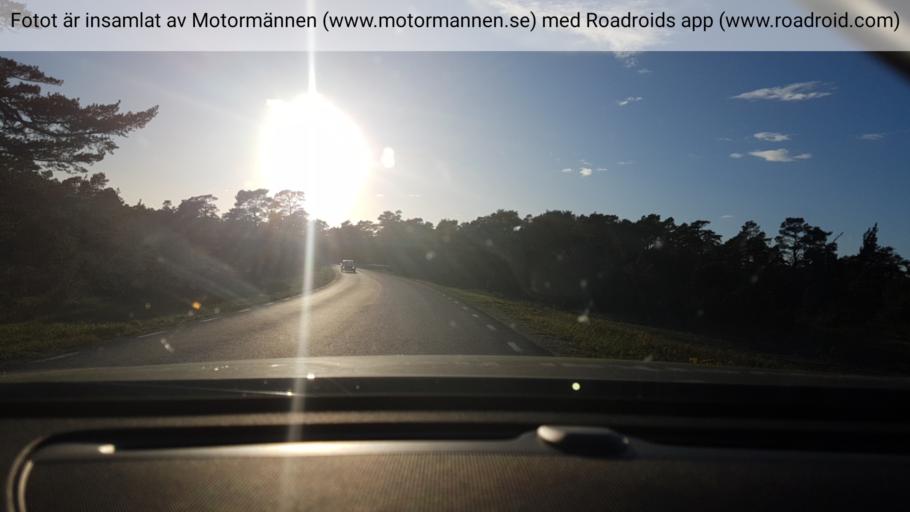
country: SE
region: Gotland
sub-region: Gotland
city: Slite
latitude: 57.8486
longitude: 18.6616
